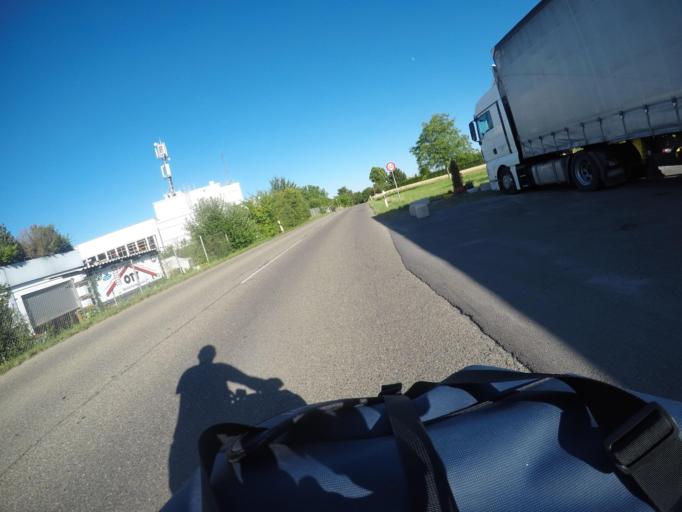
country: DE
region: Baden-Wuerttemberg
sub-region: Regierungsbezirk Stuttgart
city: Ludwigsburg
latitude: 48.8899
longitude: 9.2366
